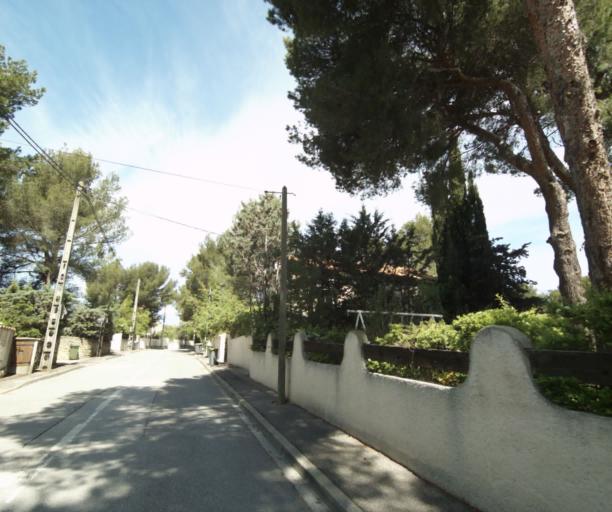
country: FR
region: Provence-Alpes-Cote d'Azur
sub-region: Departement des Bouches-du-Rhone
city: Rognac
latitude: 43.5138
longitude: 5.2208
